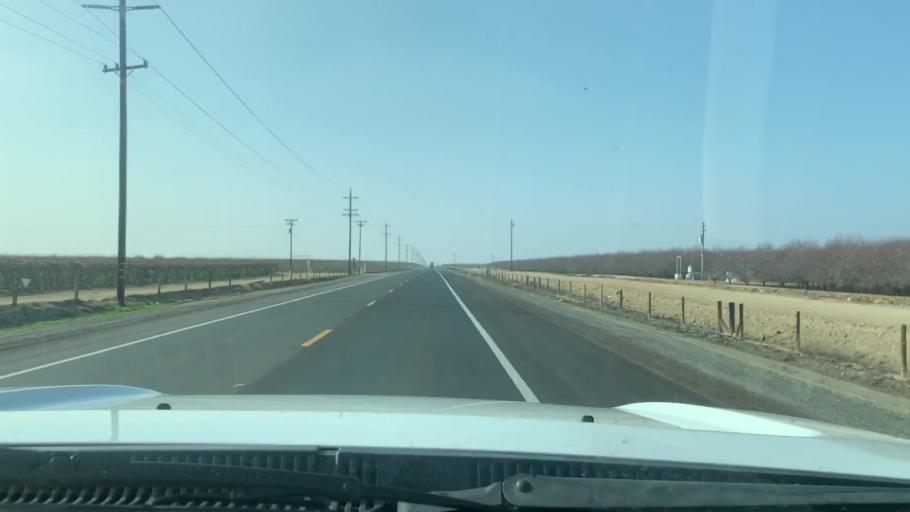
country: US
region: California
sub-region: Kern County
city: McFarland
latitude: 35.6020
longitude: -119.2312
